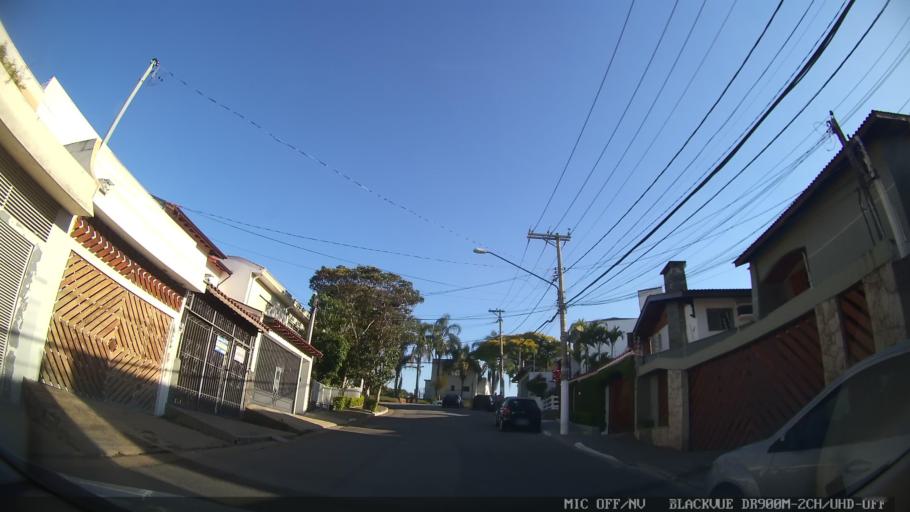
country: BR
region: Sao Paulo
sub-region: Sao Paulo
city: Sao Paulo
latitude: -23.4956
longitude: -46.6197
